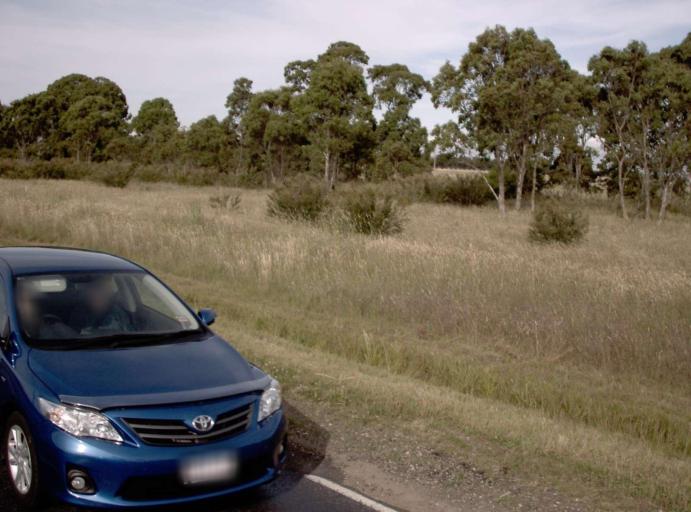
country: AU
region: Victoria
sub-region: Latrobe
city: Traralgon
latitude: -38.0753
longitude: 146.6117
